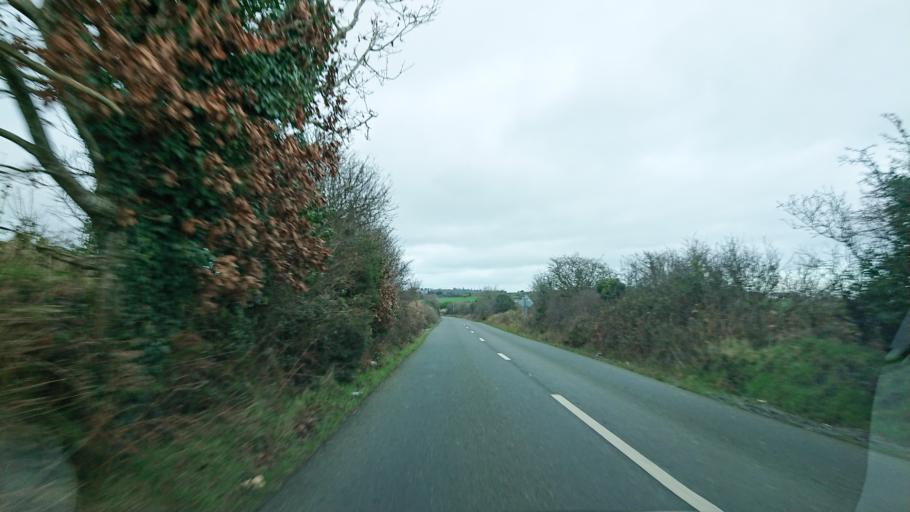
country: IE
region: Leinster
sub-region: Kilkenny
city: Mooncoin
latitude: 52.2150
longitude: -7.2410
